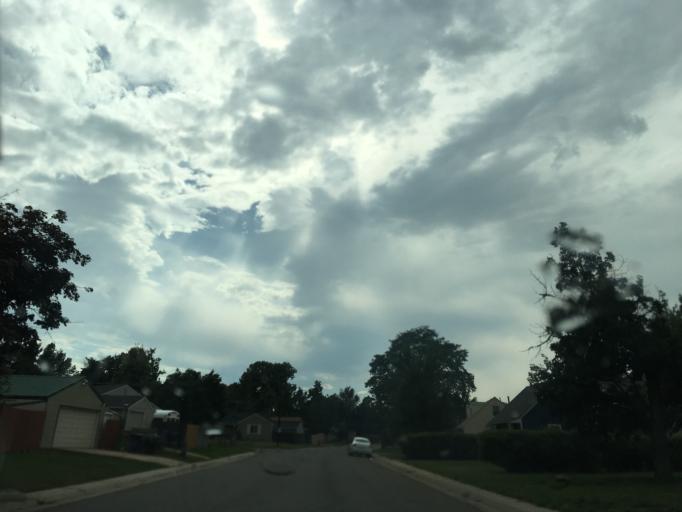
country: US
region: Colorado
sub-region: Arapahoe County
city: Sheridan
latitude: 39.6725
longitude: -105.0317
